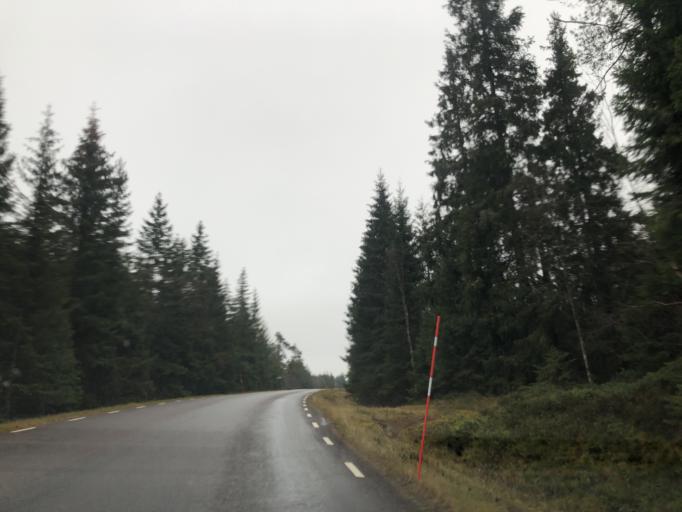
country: SE
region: Vaestra Goetaland
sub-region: Ulricehamns Kommun
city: Ulricehamn
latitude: 57.7445
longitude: 13.5348
